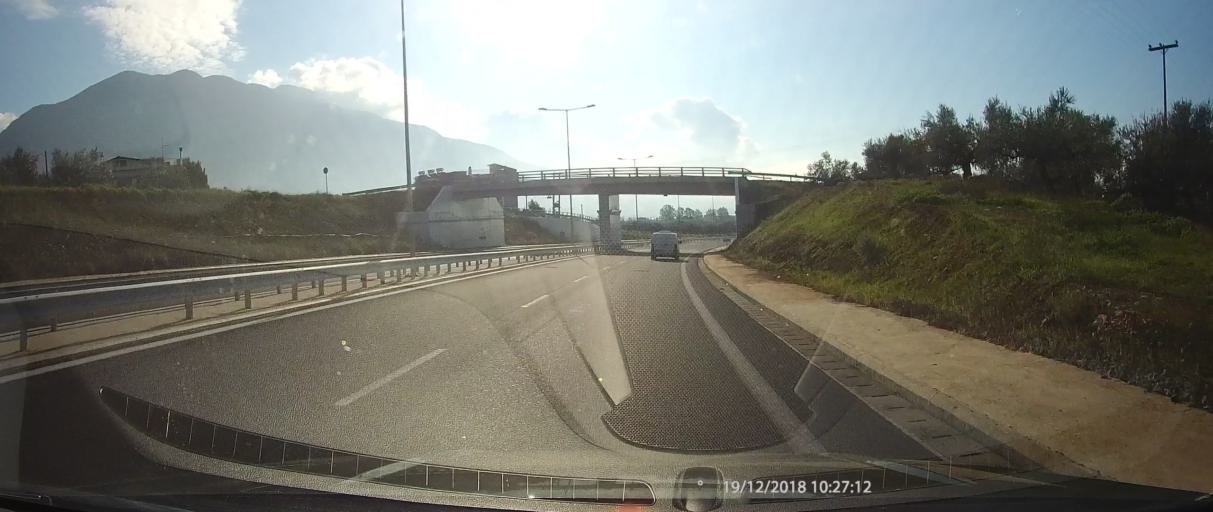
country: GR
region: Peloponnese
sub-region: Nomos Messinias
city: Kalamata
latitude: 37.0389
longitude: 22.1350
